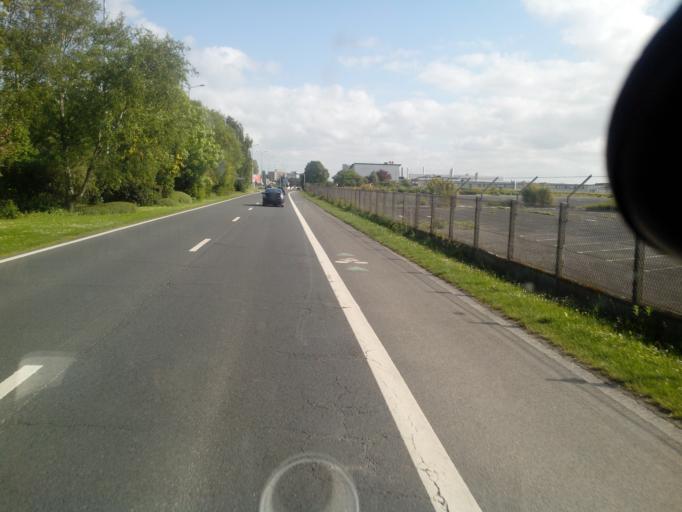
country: FR
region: Lower Normandy
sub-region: Departement du Calvados
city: Epron
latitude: 49.2081
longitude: -0.3624
